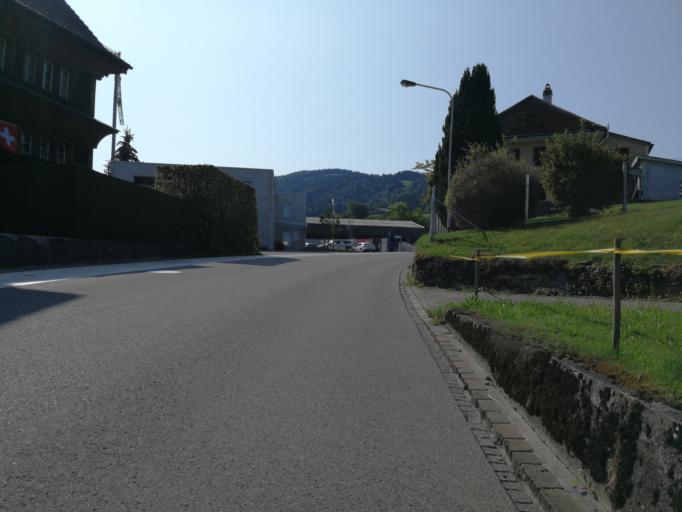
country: CH
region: Saint Gallen
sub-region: Wahlkreis Toggenburg
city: Ebnat-Kappel
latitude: 47.2578
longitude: 9.1292
